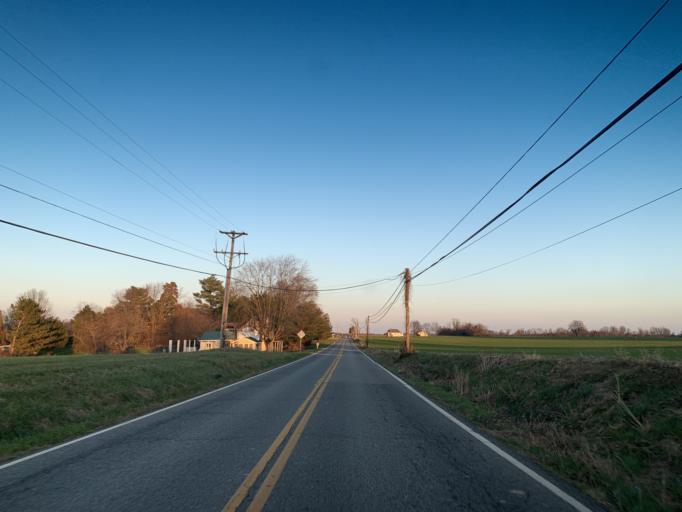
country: US
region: Maryland
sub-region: Cecil County
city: Charlestown
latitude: 39.4095
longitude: -75.9239
